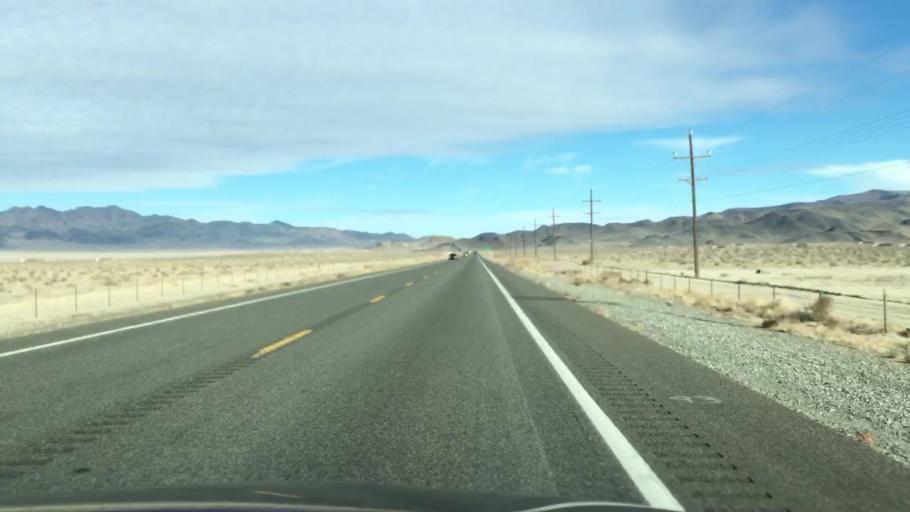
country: US
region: Nevada
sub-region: Mineral County
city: Hawthorne
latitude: 38.5273
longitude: -118.5623
